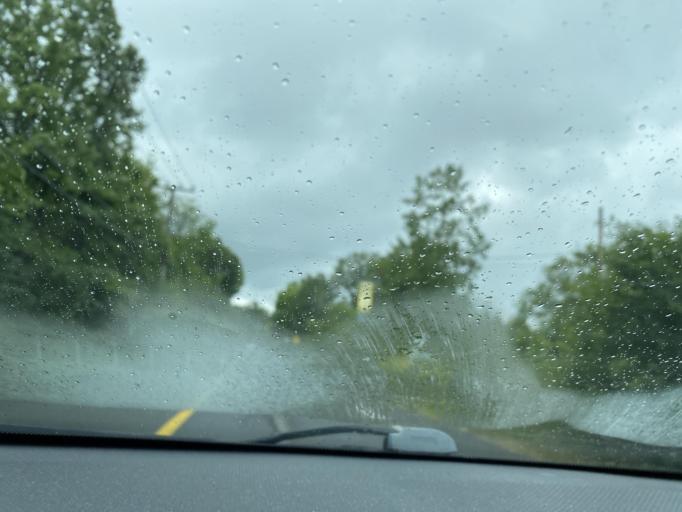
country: CA
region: Quebec
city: Baie-D'Urfe
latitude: 45.4562
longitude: -73.9327
